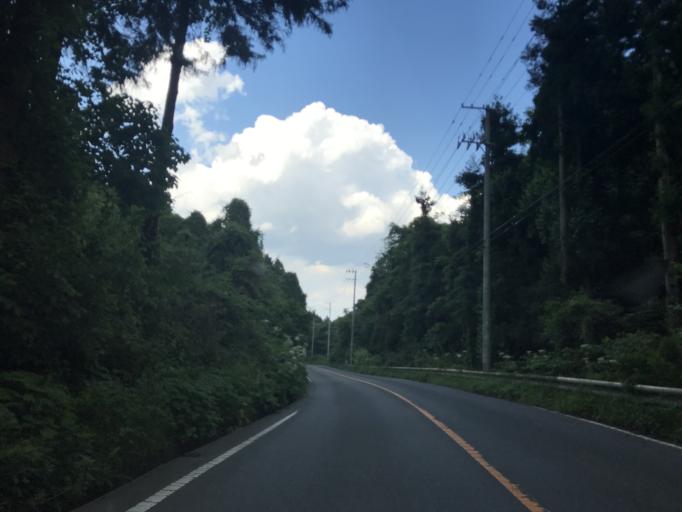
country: JP
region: Miyagi
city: Wakuya
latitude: 38.5765
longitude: 141.1449
